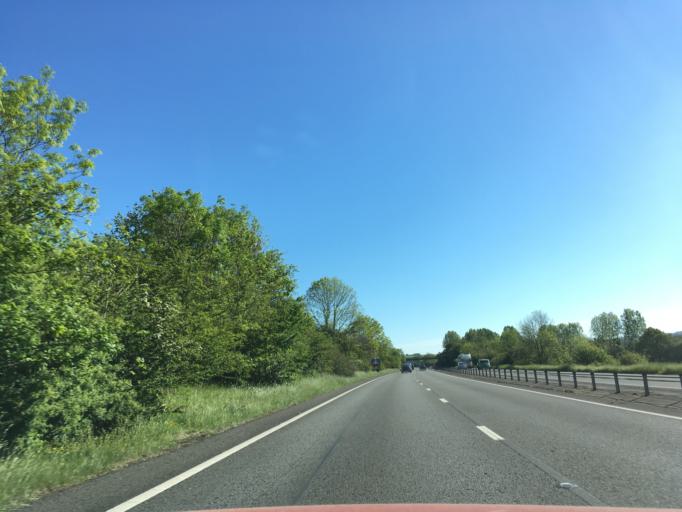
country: GB
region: Wales
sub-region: Monmouthshire
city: Llangwm
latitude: 51.7239
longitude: -2.8542
